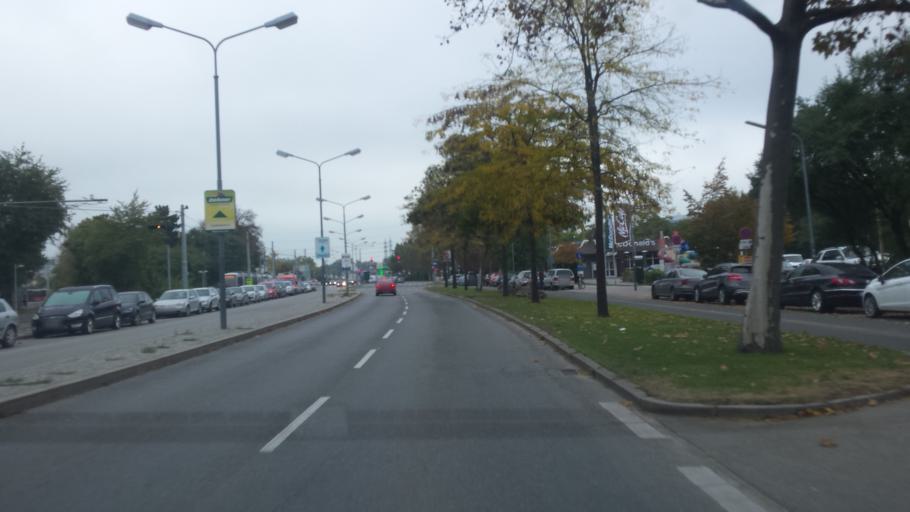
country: AT
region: Lower Austria
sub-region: Politischer Bezirk Wien-Umgebung
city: Schwechat
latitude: 48.1583
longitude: 16.4700
